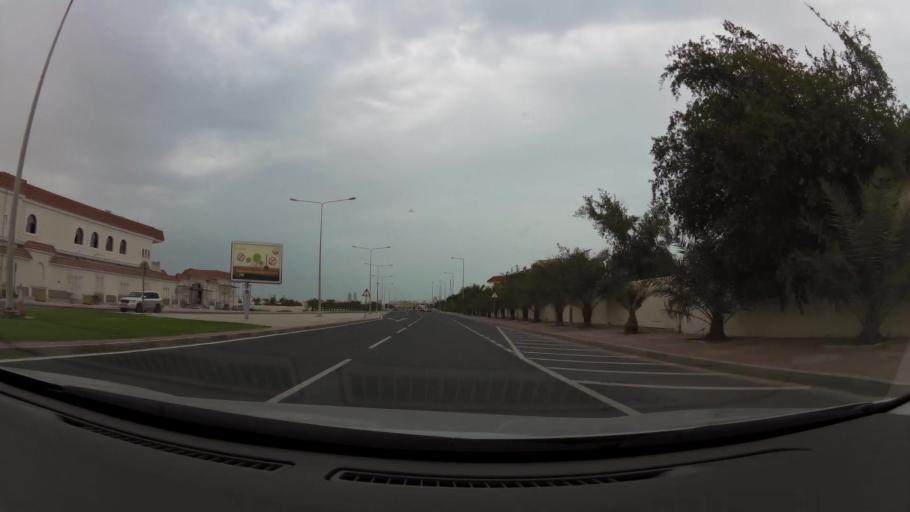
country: QA
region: Baladiyat ad Dawhah
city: Doha
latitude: 25.3252
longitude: 51.5022
